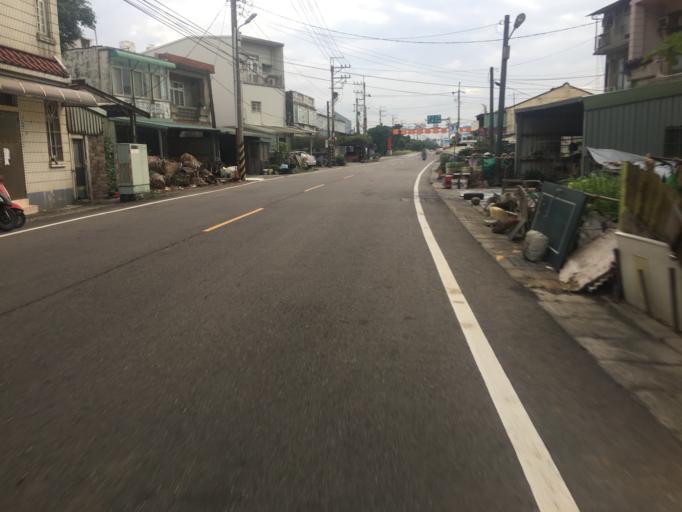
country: TW
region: Taiwan
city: Taoyuan City
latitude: 25.0954
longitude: 121.2348
